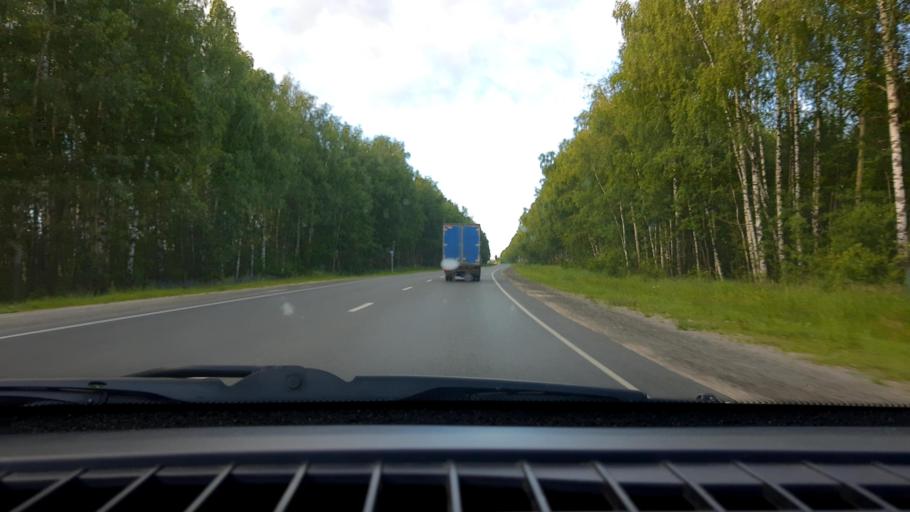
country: RU
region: Nizjnij Novgorod
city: Linda
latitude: 56.5579
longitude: 44.0245
